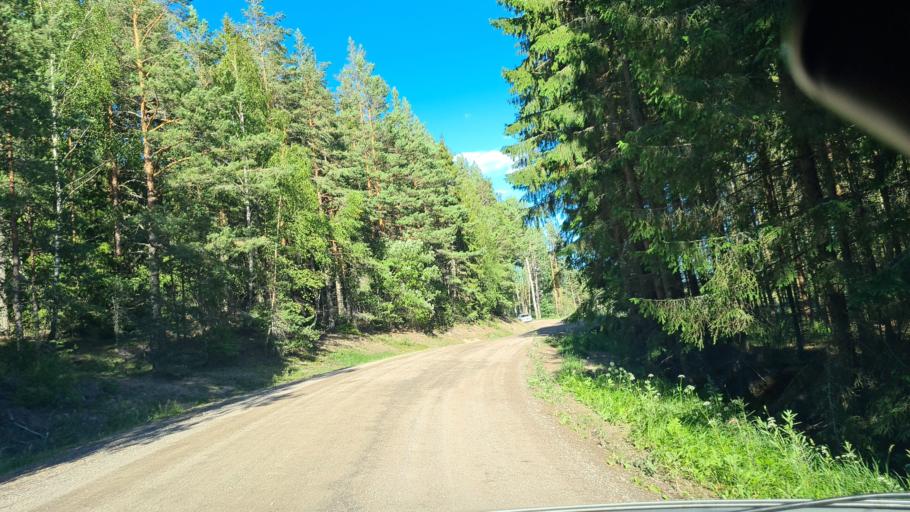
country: SE
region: Soedermanland
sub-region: Nykopings Kommun
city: Nykoping
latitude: 58.9204
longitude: 17.0393
